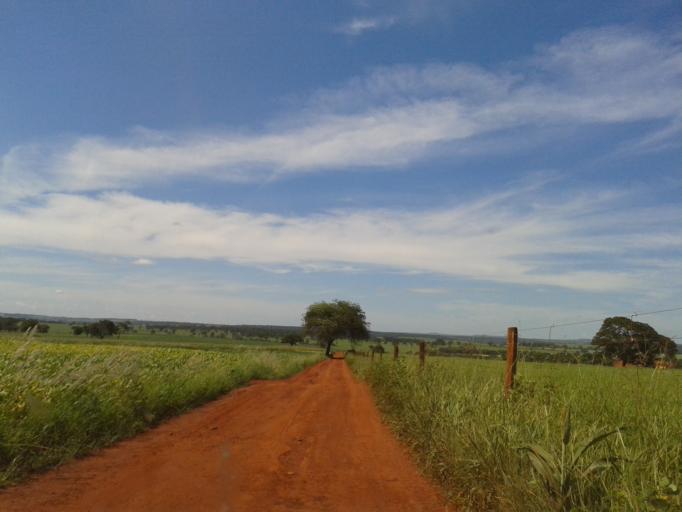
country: BR
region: Minas Gerais
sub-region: Capinopolis
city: Capinopolis
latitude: -18.7696
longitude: -49.8089
